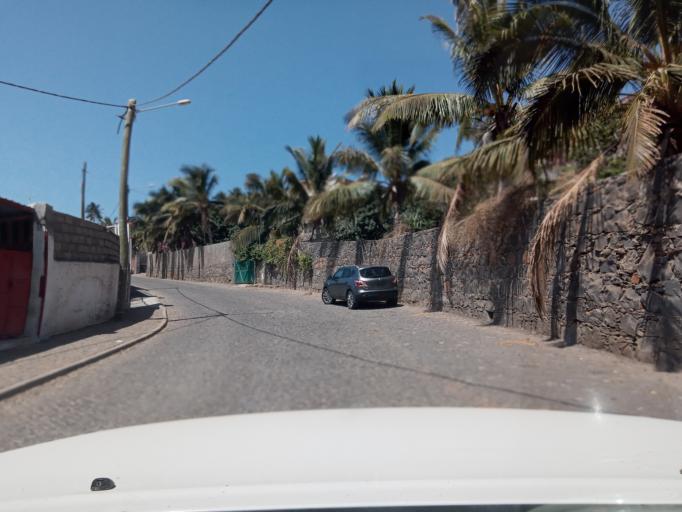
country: CV
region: Ribeira Grande de Santiago
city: Cidade Velha
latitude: 14.9168
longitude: -23.6095
